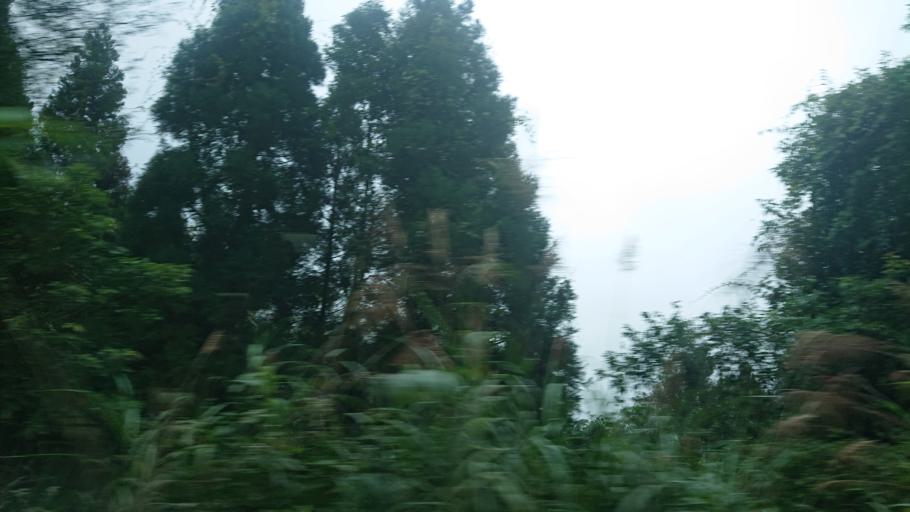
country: TW
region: Taiwan
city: Lugu
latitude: 23.6250
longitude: 120.7110
